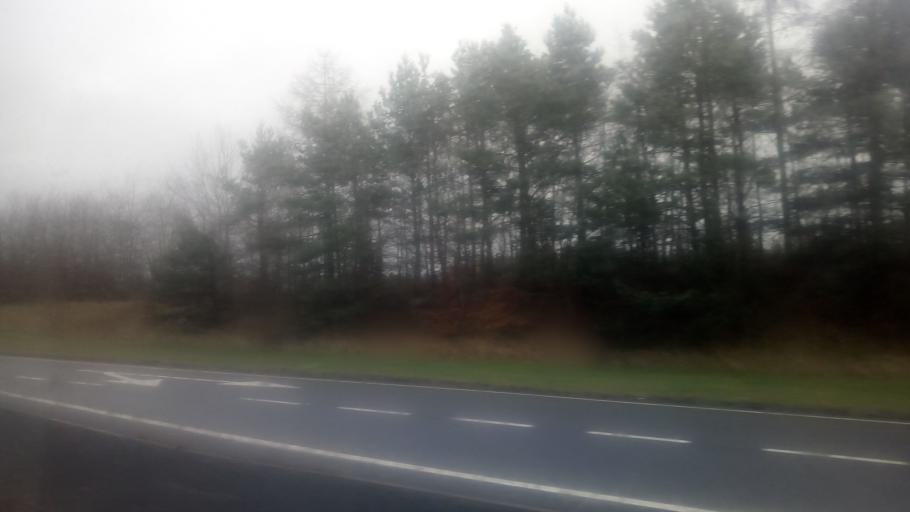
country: GB
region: Scotland
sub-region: The Scottish Borders
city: Newtown St Boswells
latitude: 55.5843
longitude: -2.6722
